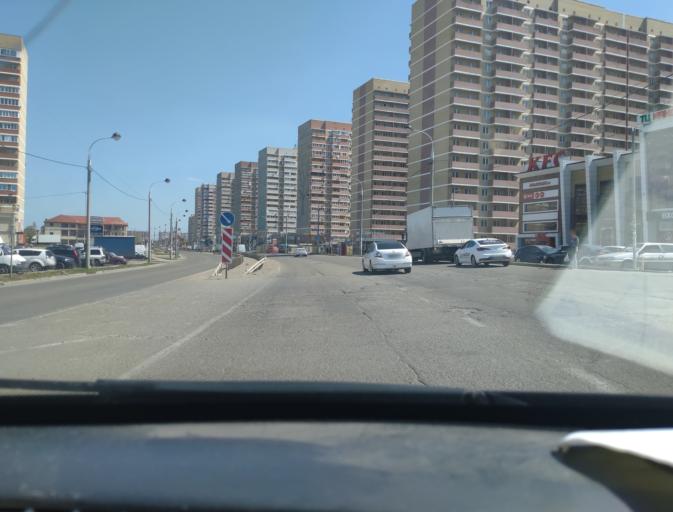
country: RU
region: Krasnodarskiy
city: Krasnodar
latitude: 45.0947
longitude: 39.0041
